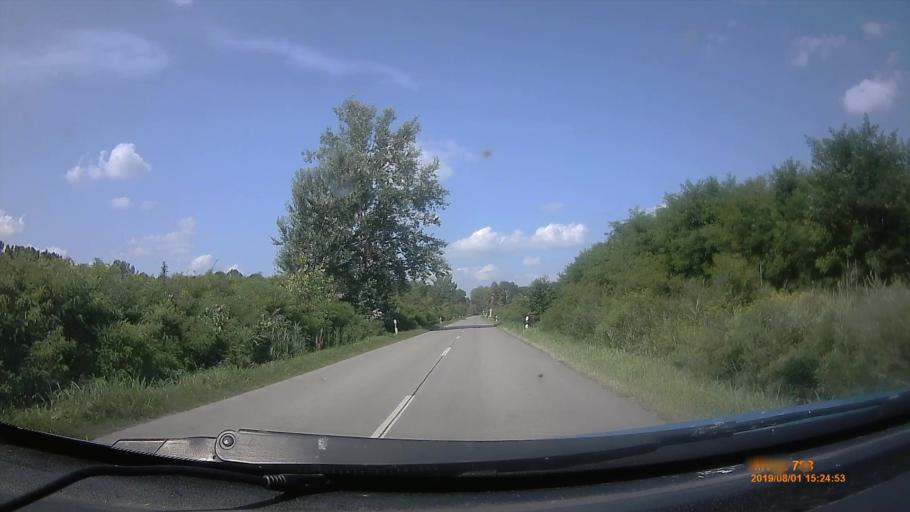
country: HU
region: Baranya
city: Sellye
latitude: 45.8887
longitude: 17.8529
